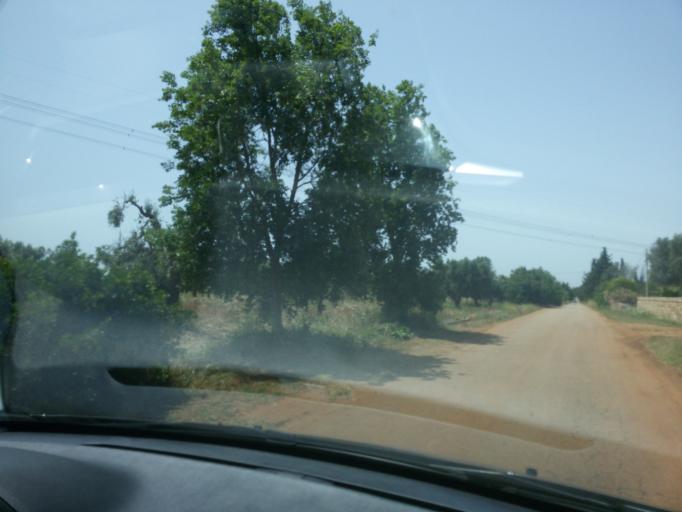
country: IT
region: Apulia
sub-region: Provincia di Lecce
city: Porto Cesareo
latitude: 40.3248
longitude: 17.8741
